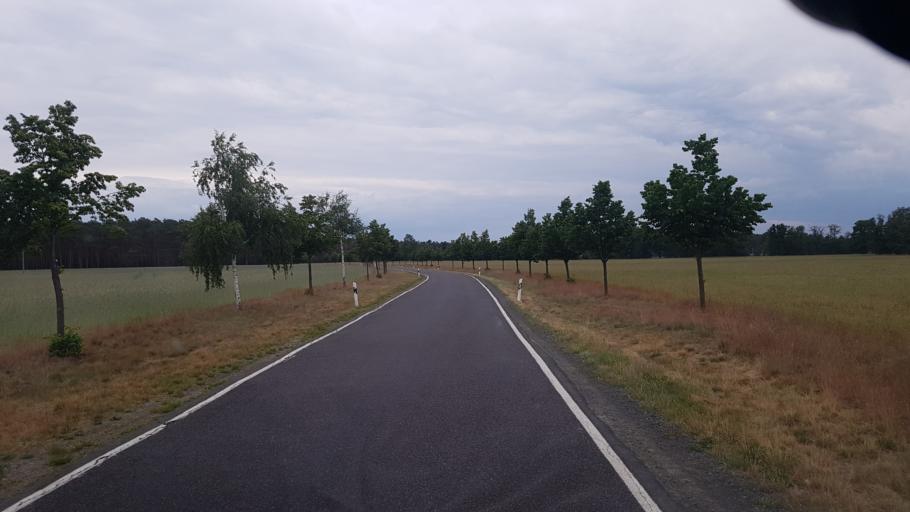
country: DE
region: Brandenburg
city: Herzberg
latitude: 51.7936
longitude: 13.2421
